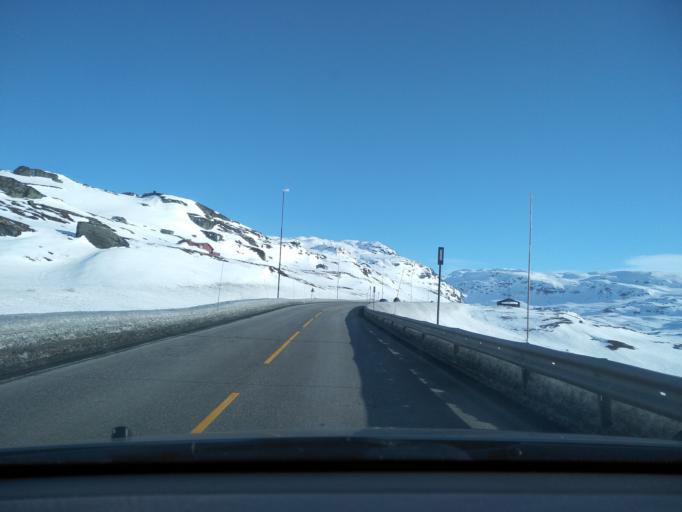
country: NO
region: Aust-Agder
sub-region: Bykle
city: Hovden
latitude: 59.8422
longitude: 6.9775
